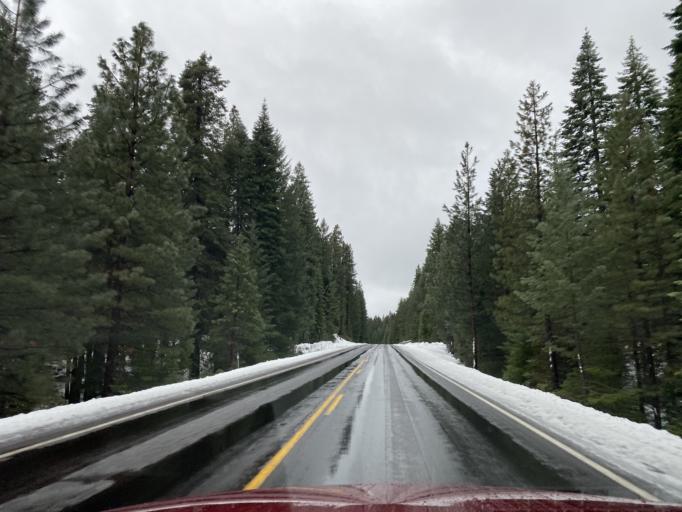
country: US
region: Oregon
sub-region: Klamath County
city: Klamath Falls
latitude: 42.5012
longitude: -122.0834
